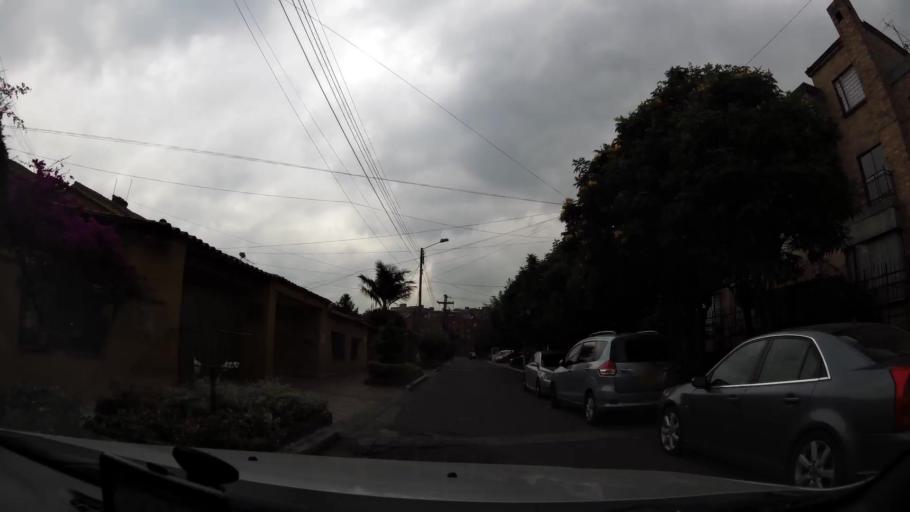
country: CO
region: Bogota D.C.
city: Bogota
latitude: 4.6649
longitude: -74.1159
